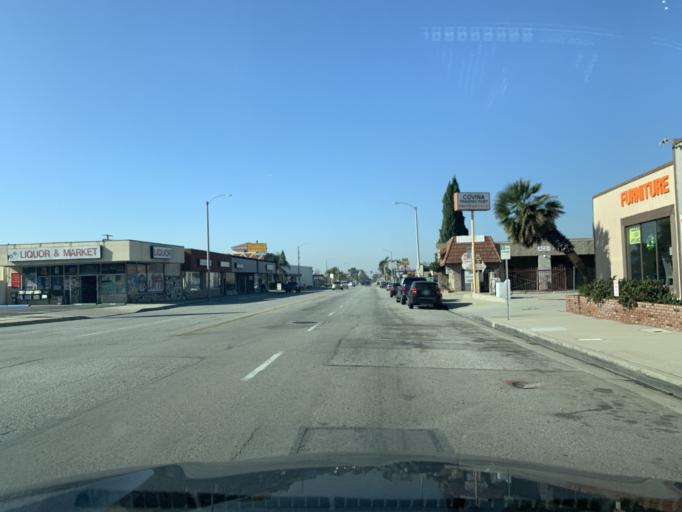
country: US
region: California
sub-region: Los Angeles County
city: Covina
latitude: 34.0910
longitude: -117.8786
